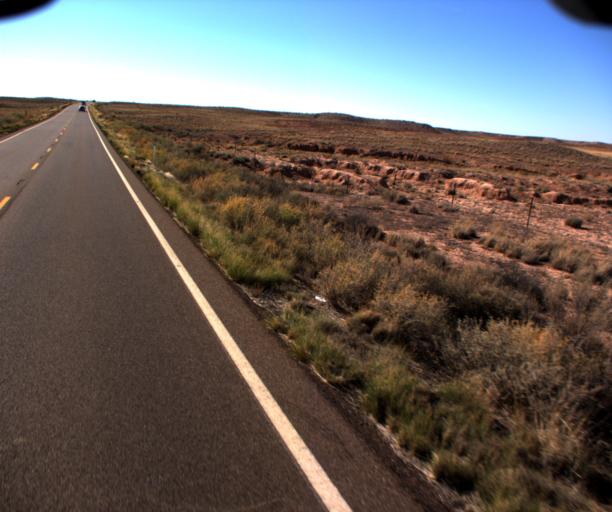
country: US
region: Arizona
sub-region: Navajo County
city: Dilkon
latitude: 35.2440
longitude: -110.4302
